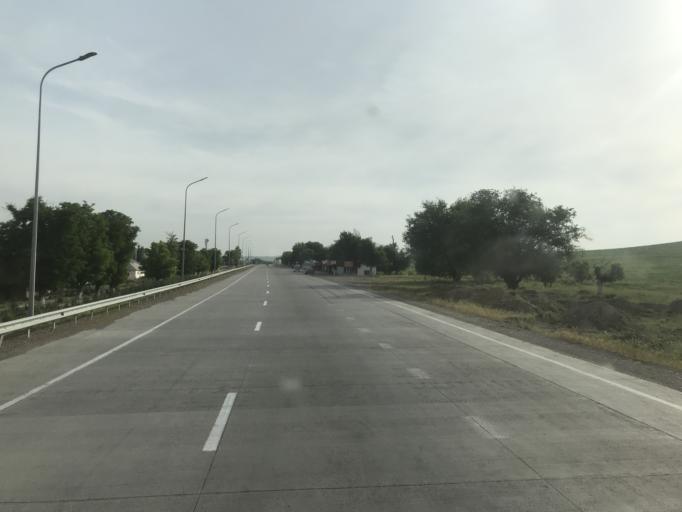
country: KZ
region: Ongtustik Qazaqstan
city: Qazyqurt
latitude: 41.9024
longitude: 69.4621
